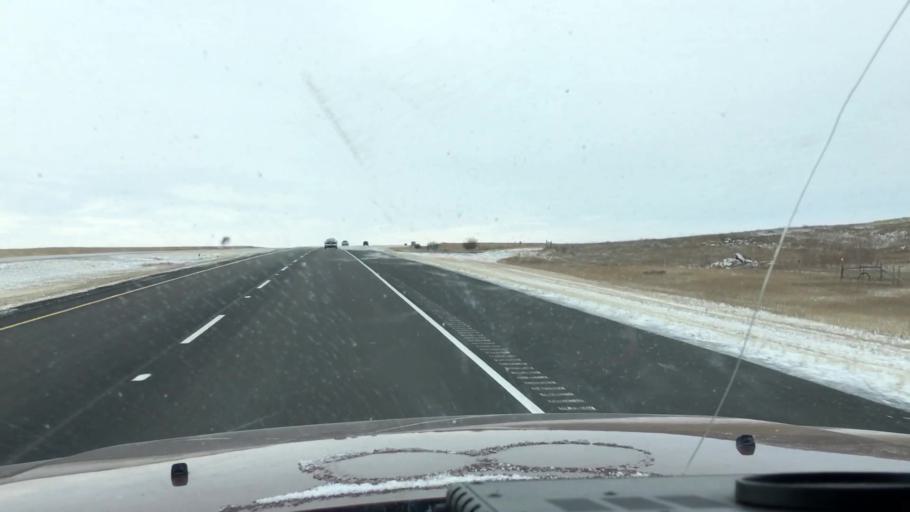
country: CA
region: Saskatchewan
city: Saskatoon
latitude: 51.7221
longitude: -106.4708
